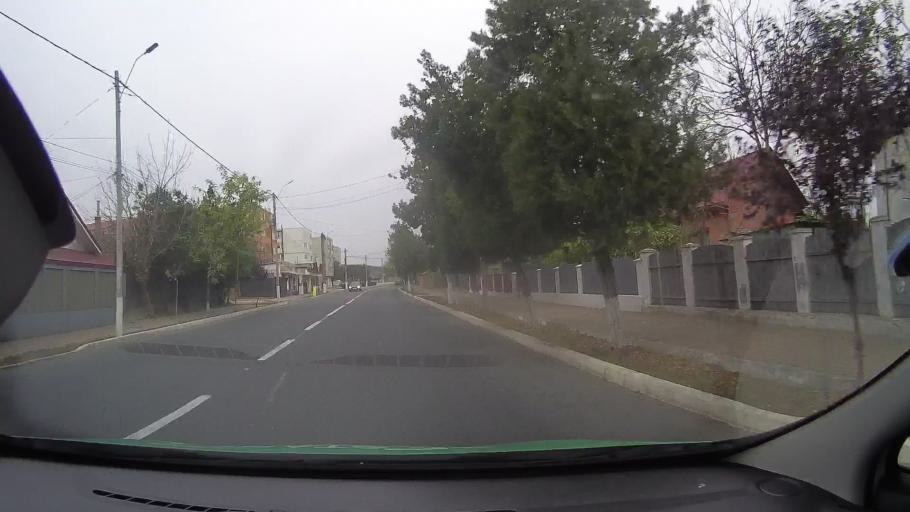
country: RO
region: Constanta
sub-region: Oras Harsova
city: Harsova
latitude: 44.6895
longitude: 27.9442
